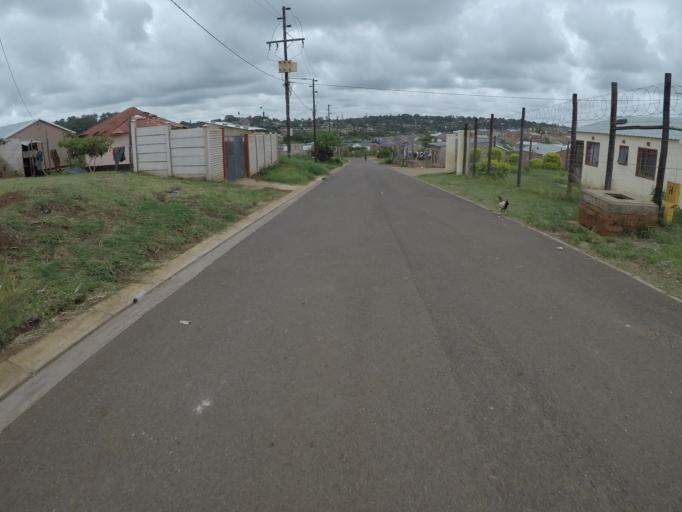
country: ZA
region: KwaZulu-Natal
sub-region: uThungulu District Municipality
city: Empangeni
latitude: -28.7640
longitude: 31.8776
